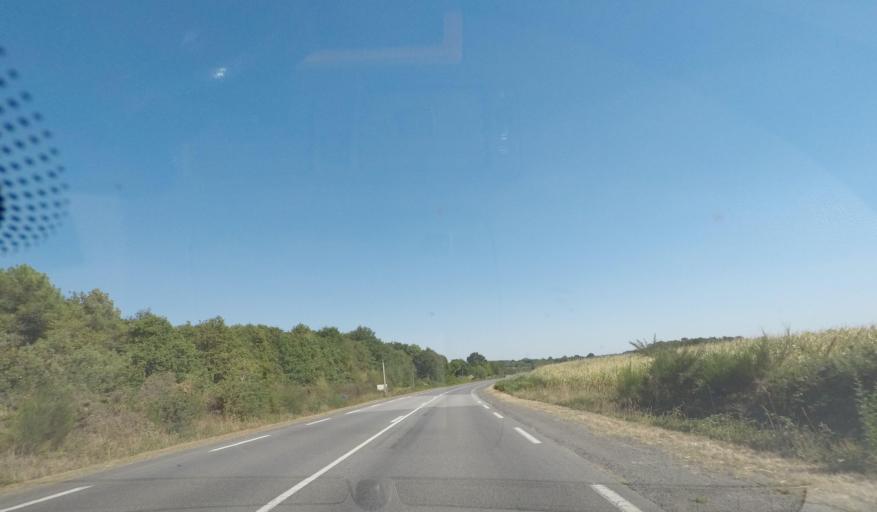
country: FR
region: Brittany
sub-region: Departement du Morbihan
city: Questembert
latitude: 47.6333
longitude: -2.4167
